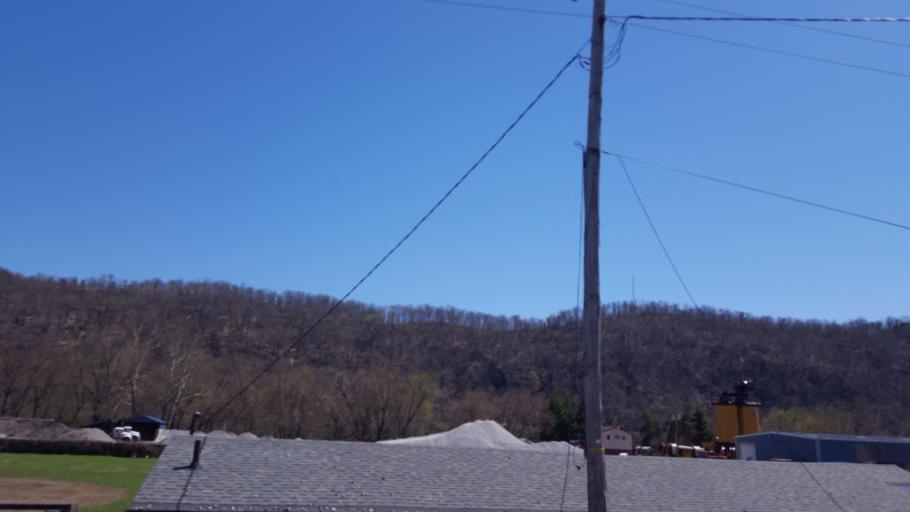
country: US
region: Ohio
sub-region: Belmont County
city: Martins Ferry
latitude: 40.0994
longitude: -80.7143
